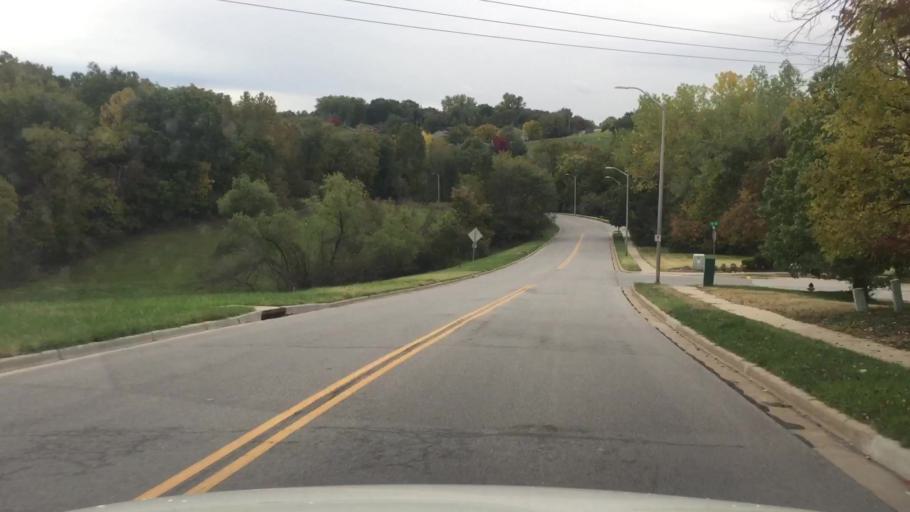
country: US
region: Kansas
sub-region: Johnson County
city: Shawnee
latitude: 39.0268
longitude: -94.7443
